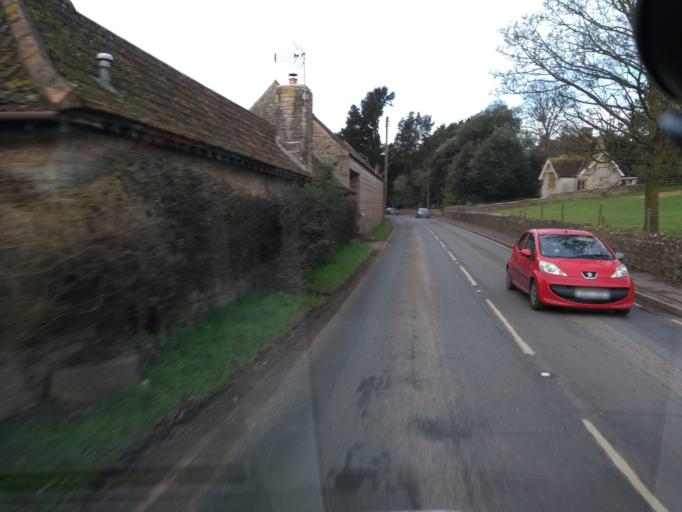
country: GB
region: England
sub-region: Somerset
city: Langport
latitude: 51.1236
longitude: -2.8384
